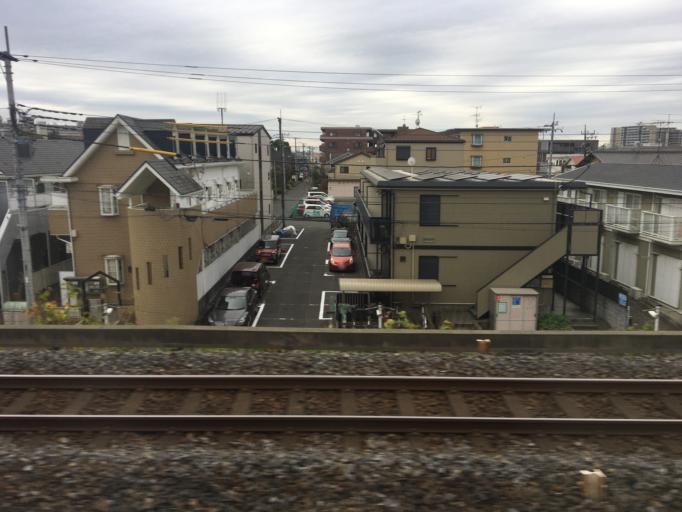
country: JP
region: Chiba
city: Nagareyama
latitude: 35.8359
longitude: 139.9059
